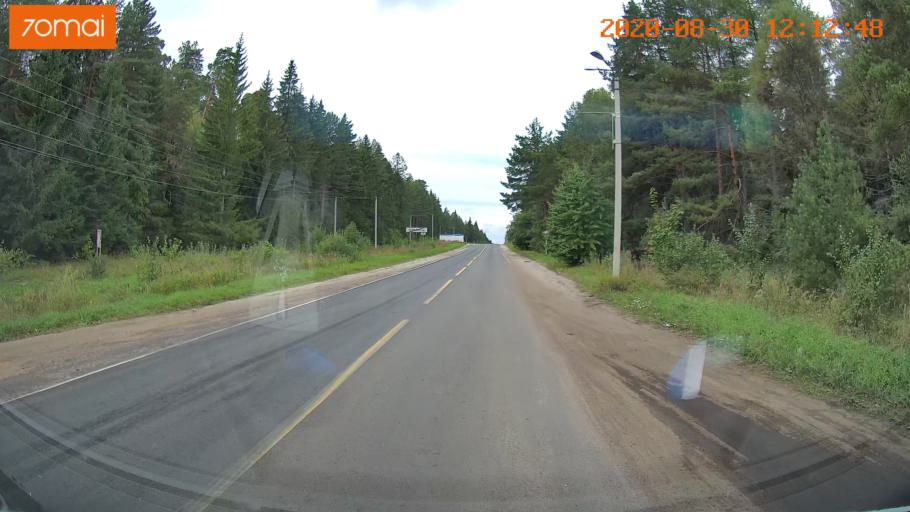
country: RU
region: Ivanovo
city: Yur'yevets
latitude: 57.3117
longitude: 43.0892
